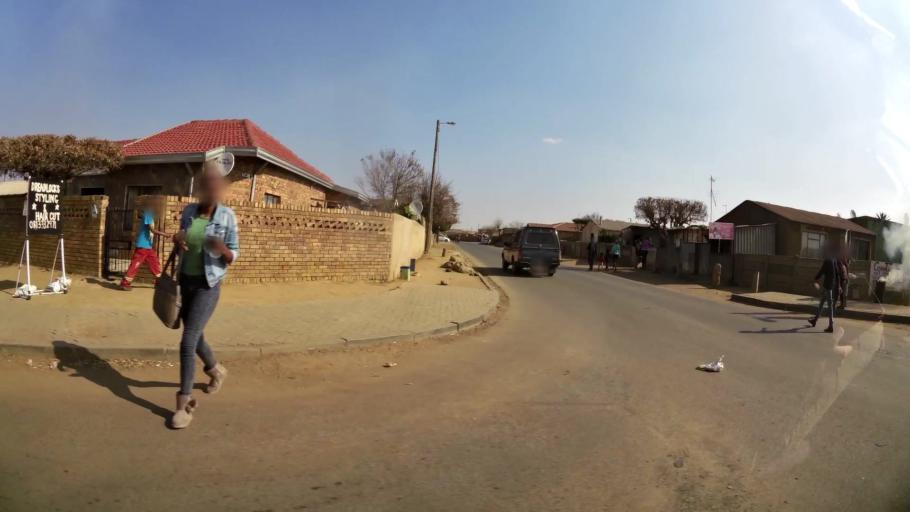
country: ZA
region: Gauteng
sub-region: Ekurhuleni Metropolitan Municipality
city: Brakpan
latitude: -26.1367
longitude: 28.4273
